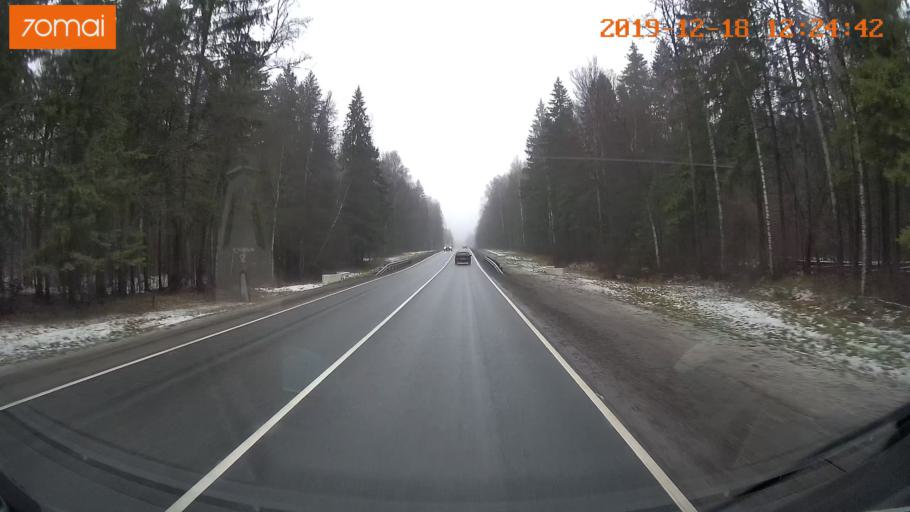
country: RU
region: Moskovskaya
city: Novopetrovskoye
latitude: 56.0282
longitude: 36.5007
